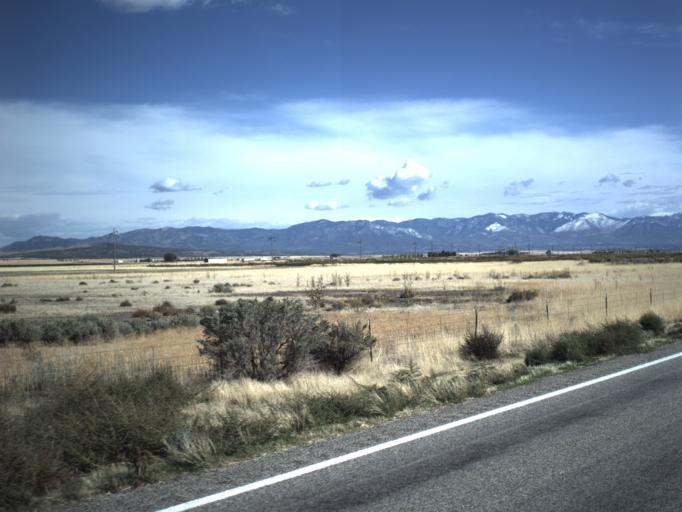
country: US
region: Utah
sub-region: Millard County
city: Delta
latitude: 39.2207
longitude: -112.4207
